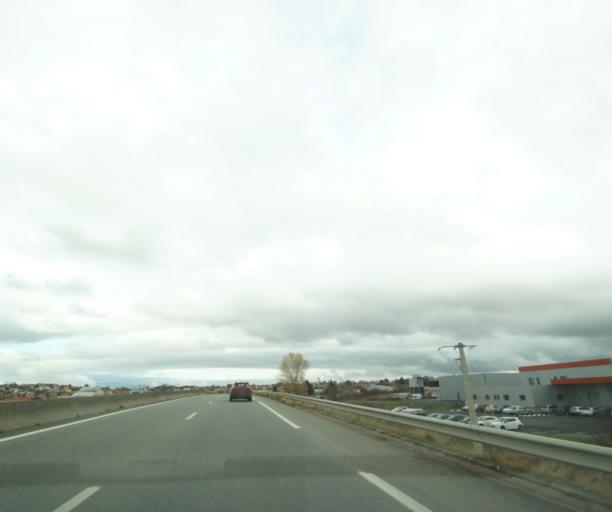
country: FR
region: Auvergne
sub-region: Departement du Puy-de-Dome
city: Dallet
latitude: 45.7884
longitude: 3.2217
